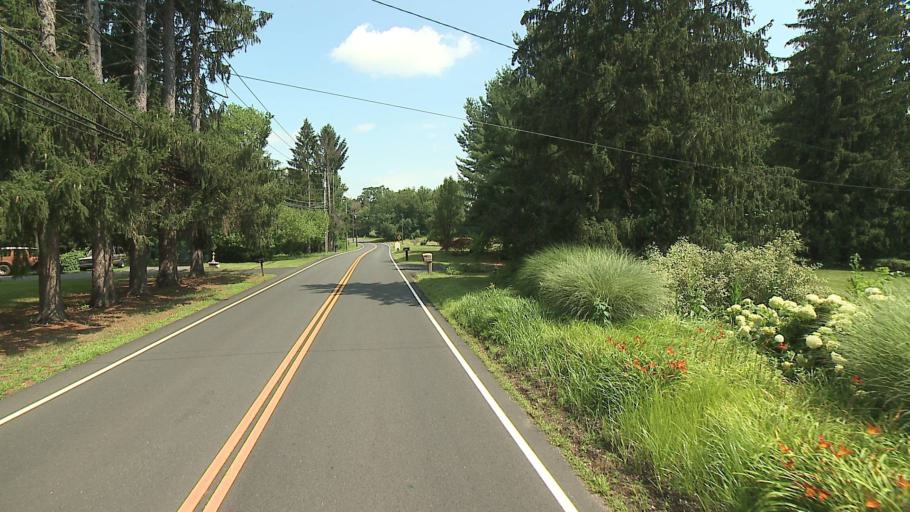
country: US
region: Connecticut
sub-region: Hartford County
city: Collinsville
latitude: 41.8004
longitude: -72.8893
